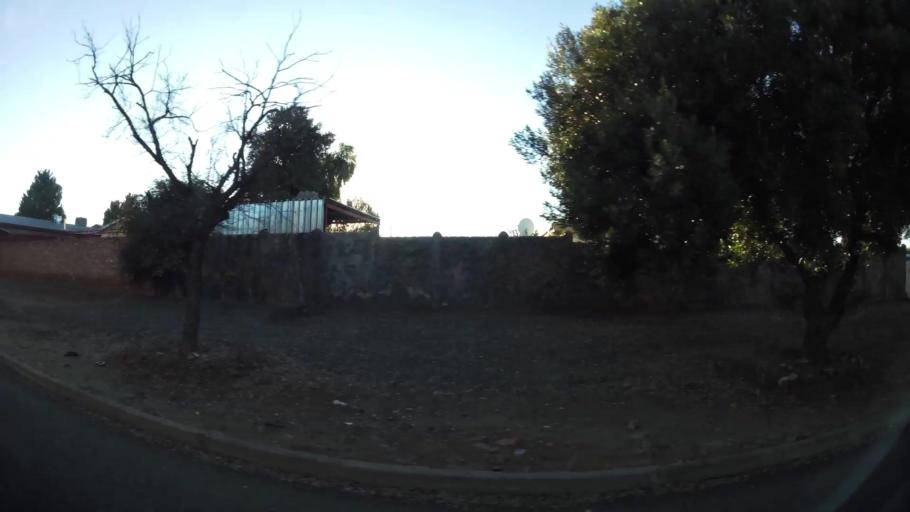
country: ZA
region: Northern Cape
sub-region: Frances Baard District Municipality
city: Kimberley
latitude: -28.7706
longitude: 24.7623
